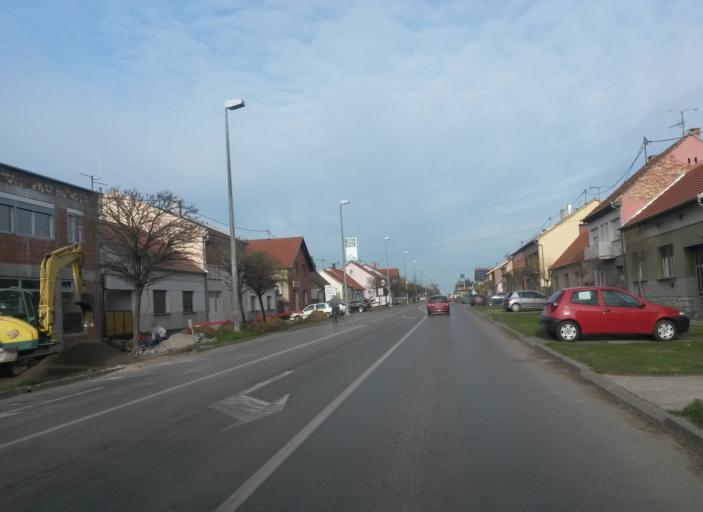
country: HR
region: Osjecko-Baranjska
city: Viskovci
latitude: 45.3194
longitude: 18.4162
